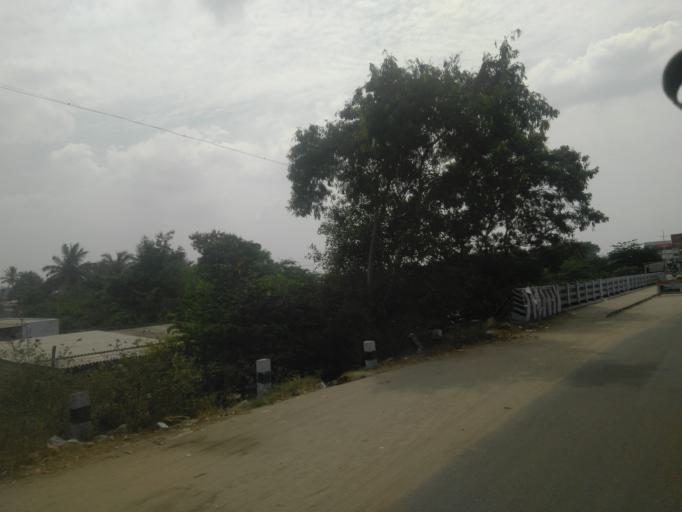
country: IN
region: Tamil Nadu
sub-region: Coimbatore
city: Irugur
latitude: 11.0039
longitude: 77.0647
